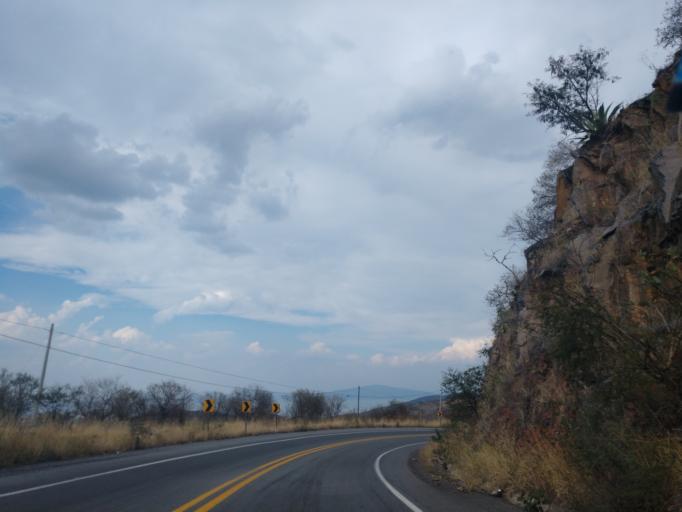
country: MX
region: Jalisco
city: La Manzanilla de la Paz
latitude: 20.1035
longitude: -103.1705
